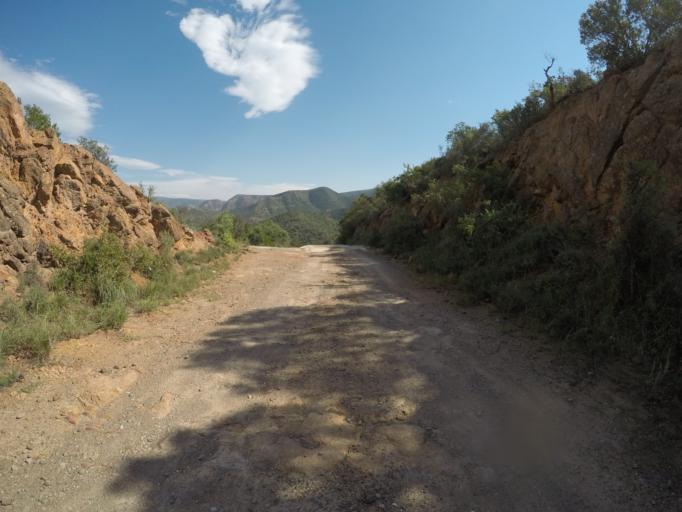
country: ZA
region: Eastern Cape
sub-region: Cacadu District Municipality
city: Kareedouw
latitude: -33.6544
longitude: 24.4242
